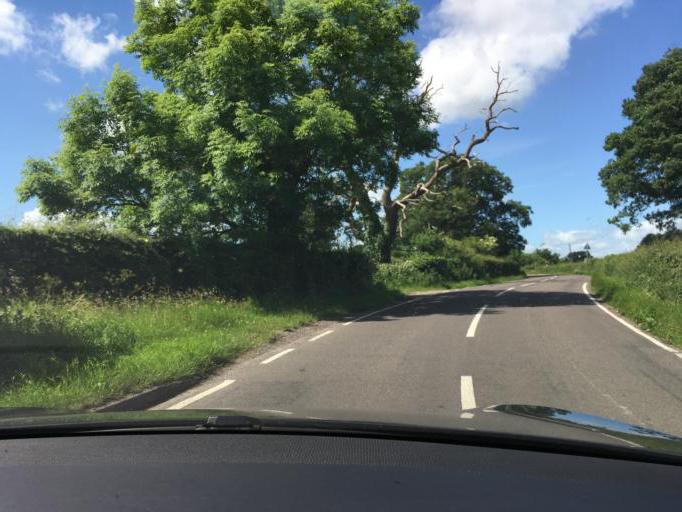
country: GB
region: England
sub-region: Cheshire East
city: Mobberley
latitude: 53.3233
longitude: -2.2908
